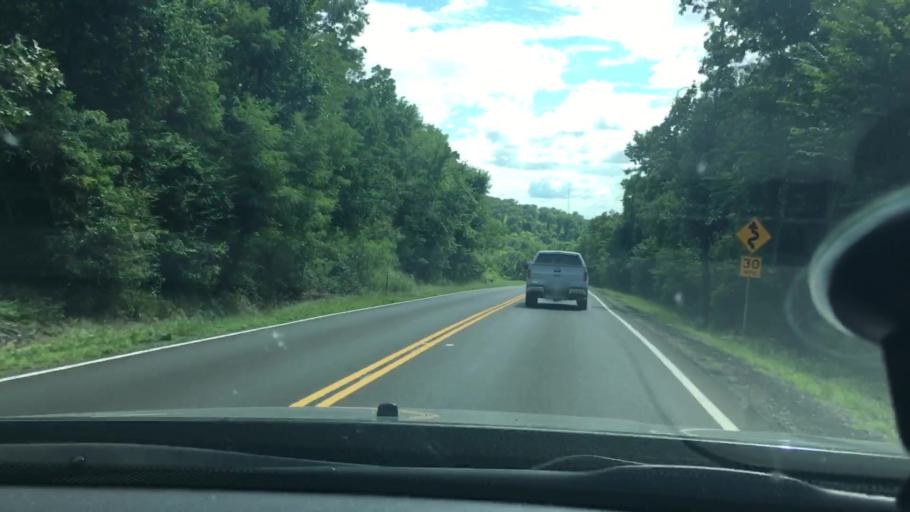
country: US
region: Oklahoma
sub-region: Sequoyah County
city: Vian
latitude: 35.6537
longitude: -94.9526
